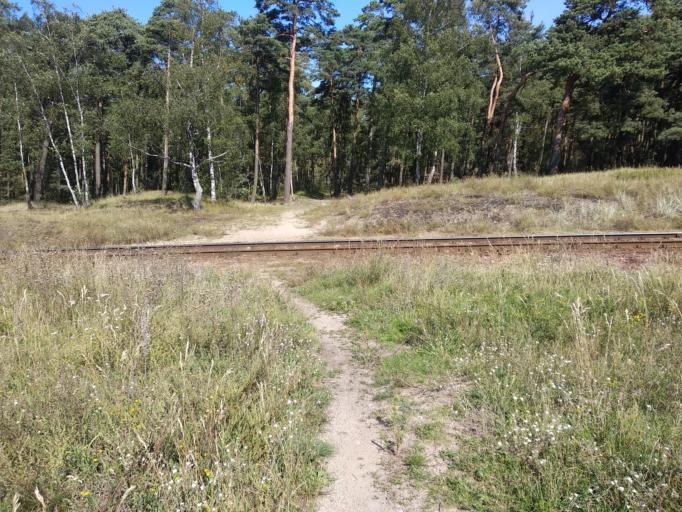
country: LT
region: Klaipedos apskritis
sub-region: Klaipeda
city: Klaipeda
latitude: 55.7285
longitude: 21.1102
